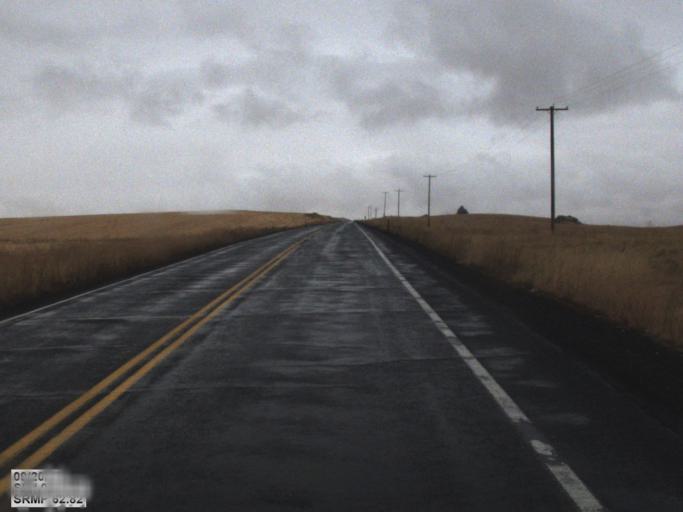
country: US
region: Washington
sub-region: Lincoln County
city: Davenport
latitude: 47.4784
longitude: -118.1968
